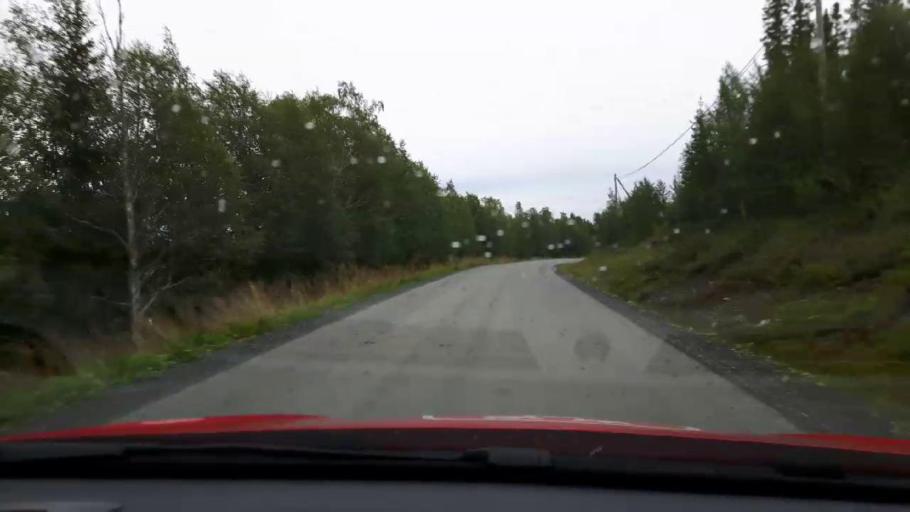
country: SE
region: Jaemtland
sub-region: Are Kommun
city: Are
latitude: 63.4797
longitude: 13.1544
